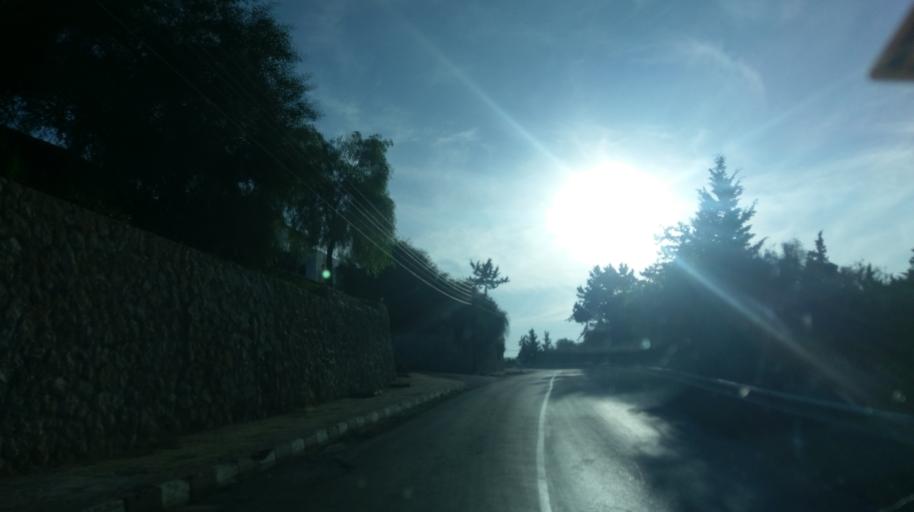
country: CY
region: Ammochostos
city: Lefkonoiko
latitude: 35.3430
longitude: 33.5793
